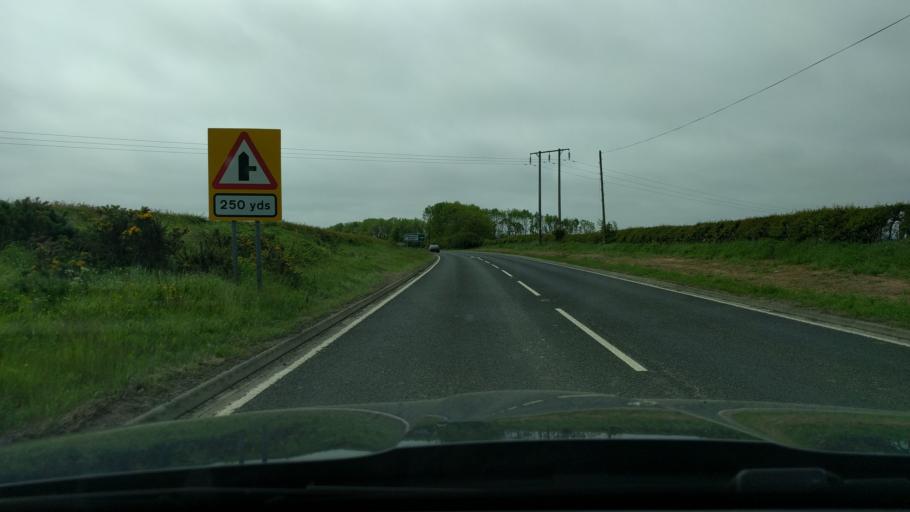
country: GB
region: England
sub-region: Northumberland
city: East Chevington
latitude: 55.2373
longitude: -1.5926
